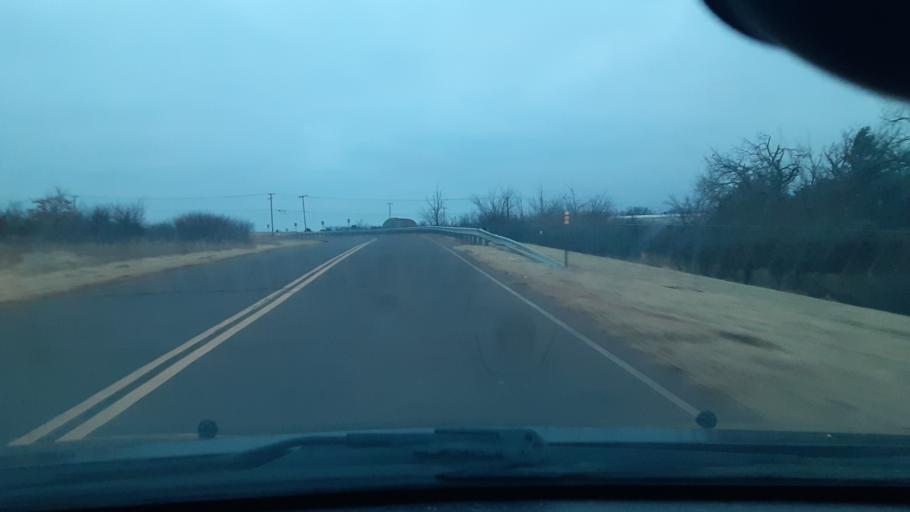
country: US
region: Oklahoma
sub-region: Logan County
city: Guthrie
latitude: 35.8576
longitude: -97.4144
